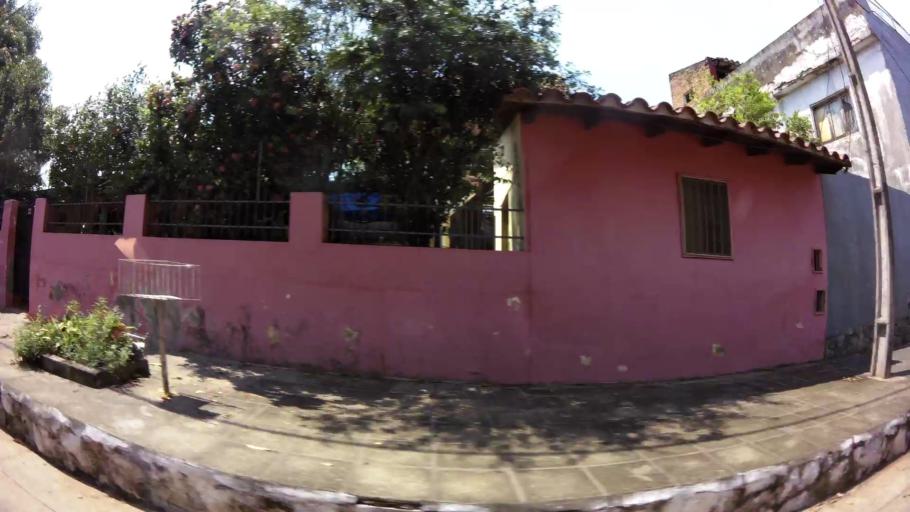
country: PY
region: Asuncion
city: Asuncion
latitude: -25.2970
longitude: -57.6523
